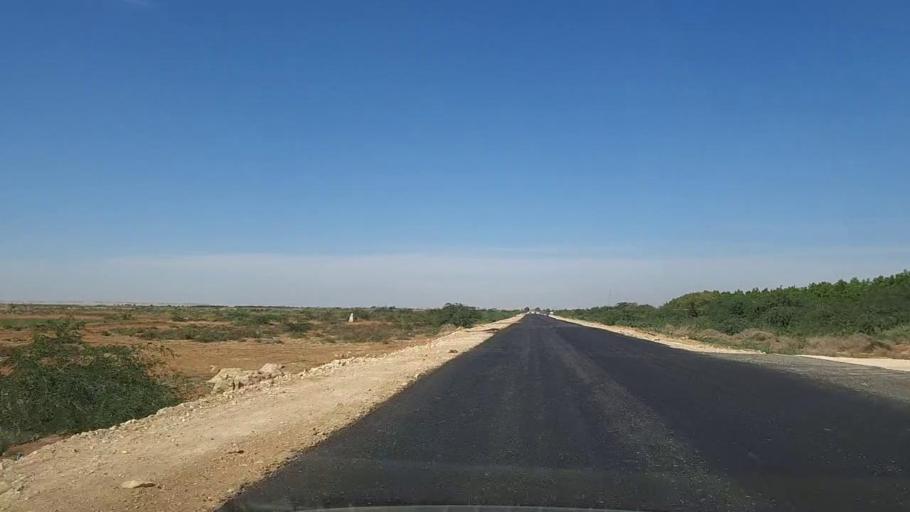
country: PK
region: Sindh
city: Kotri
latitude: 25.2365
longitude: 68.2326
